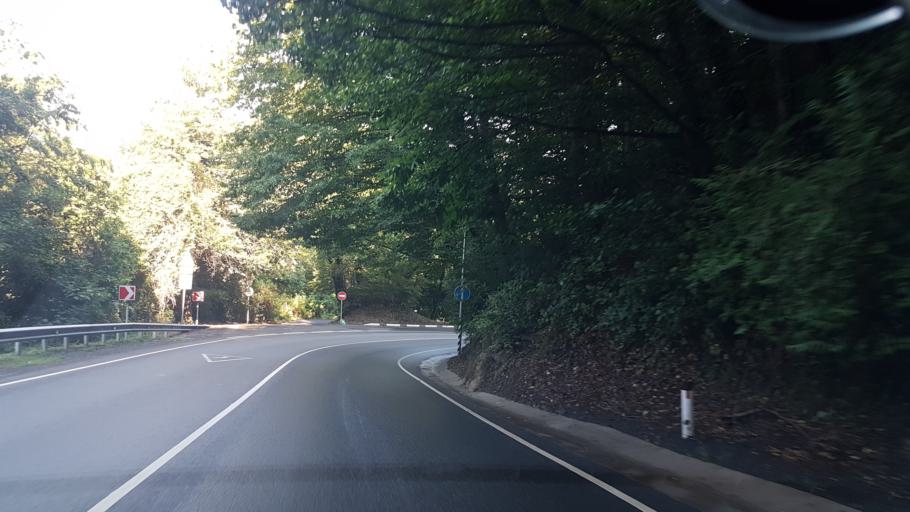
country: RU
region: Krasnodarskiy
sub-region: Sochi City
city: Lazarevskoye
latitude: 43.8703
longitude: 39.3985
